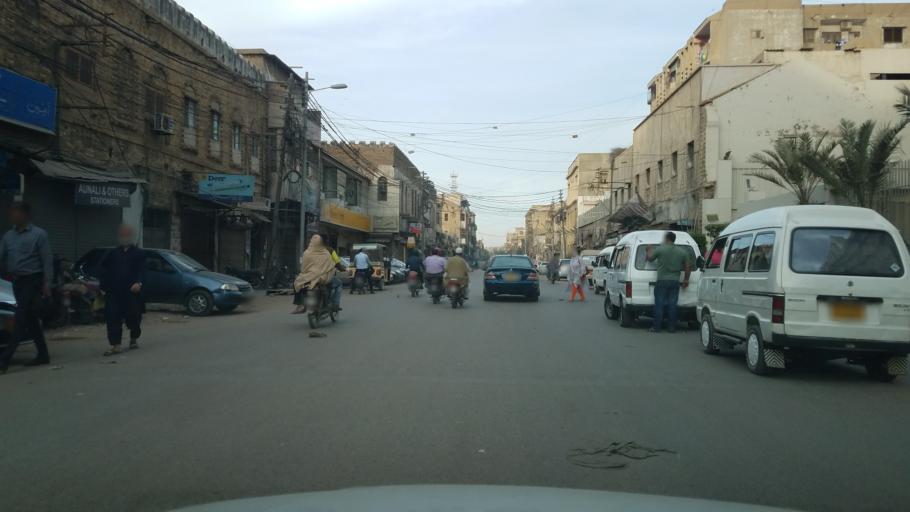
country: PK
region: Sindh
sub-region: Karachi District
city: Karachi
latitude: 24.8528
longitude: 67.0073
